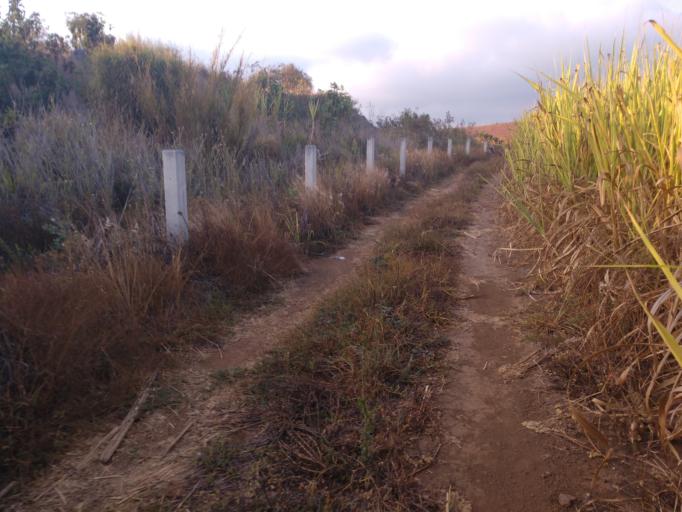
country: MX
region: Nayarit
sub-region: Tepic
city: La Corregidora
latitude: 21.4852
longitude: -104.8103
